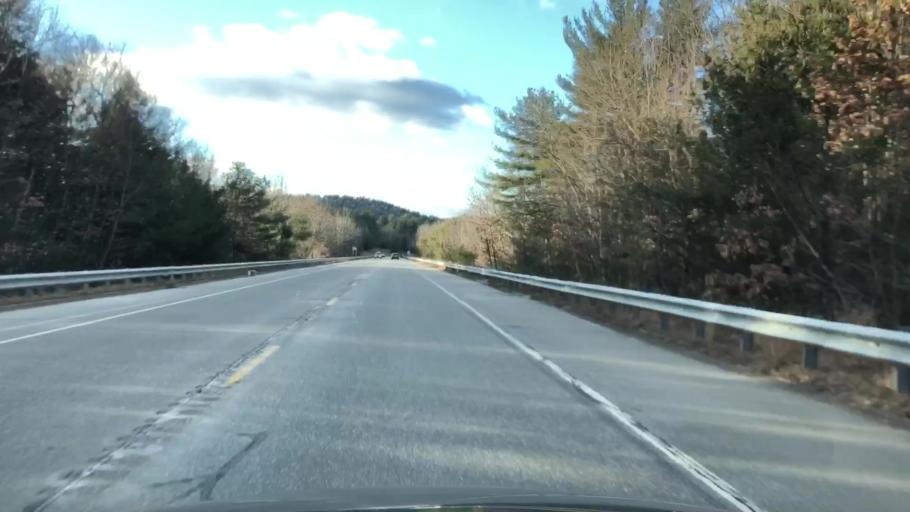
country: US
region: New Hampshire
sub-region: Hillsborough County
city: Wilton
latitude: 42.8344
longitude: -71.6935
